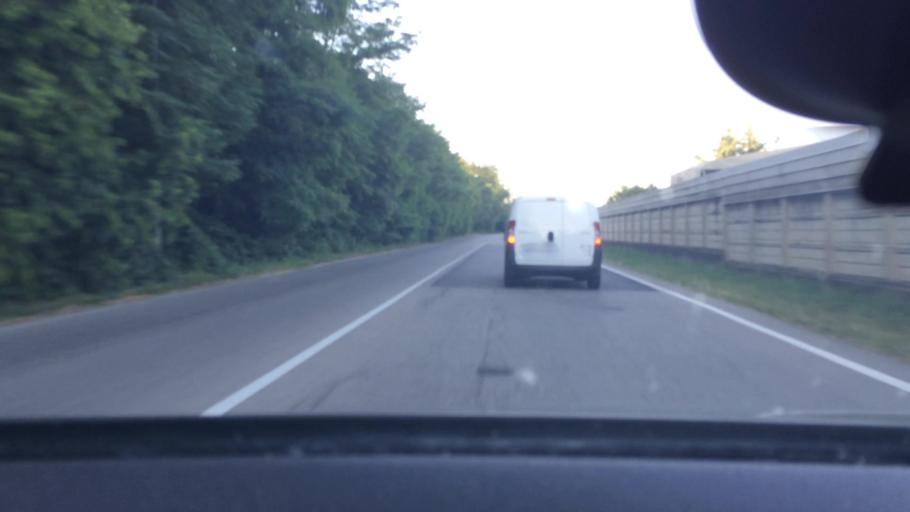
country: IT
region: Lombardy
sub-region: Citta metropolitana di Milano
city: Rescaldina
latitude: 45.6254
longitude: 8.9616
